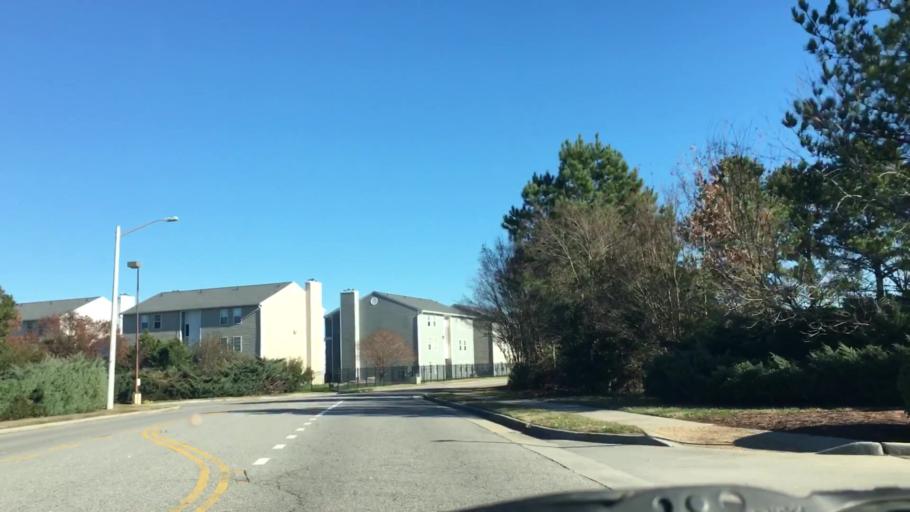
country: US
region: Virginia
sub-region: City of Virginia Beach
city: Virginia Beach
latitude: 36.8517
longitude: -76.0266
